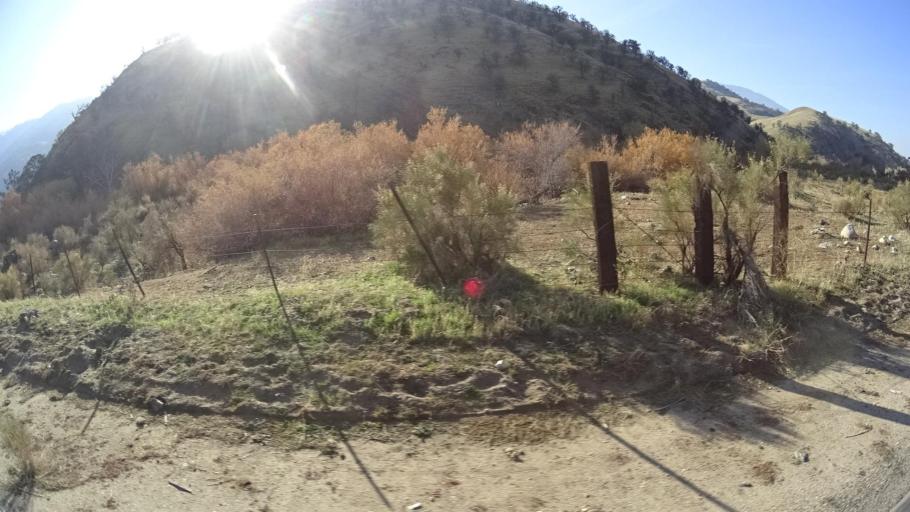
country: US
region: California
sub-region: Kern County
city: Bear Valley Springs
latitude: 35.3010
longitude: -118.6005
